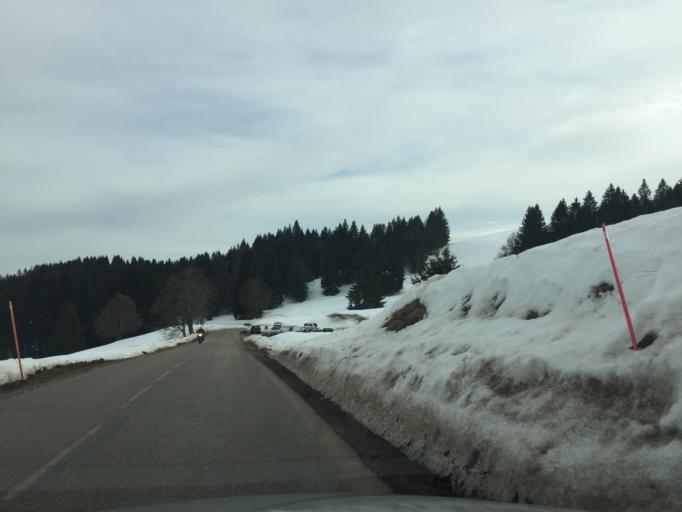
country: FR
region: Rhone-Alpes
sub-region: Departement de la Savoie
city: Mouxy
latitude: 45.6709
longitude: 5.9727
